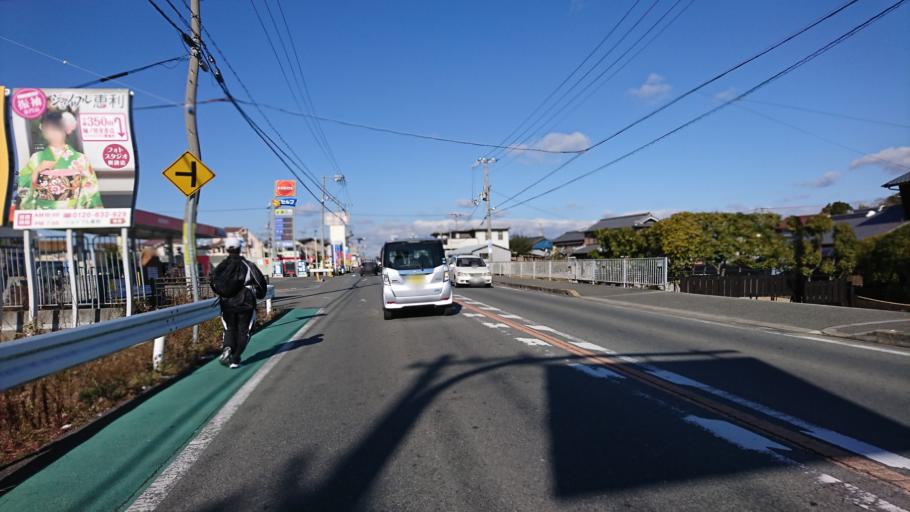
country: JP
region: Hyogo
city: Kakogawacho-honmachi
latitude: 34.7338
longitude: 134.8764
